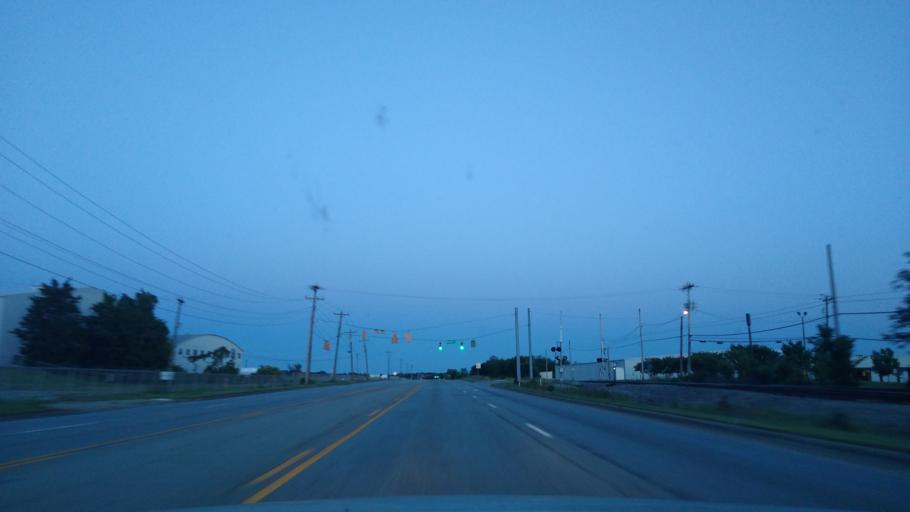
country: US
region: North Carolina
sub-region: Guilford County
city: Jamestown
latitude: 36.0878
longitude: -79.9435
